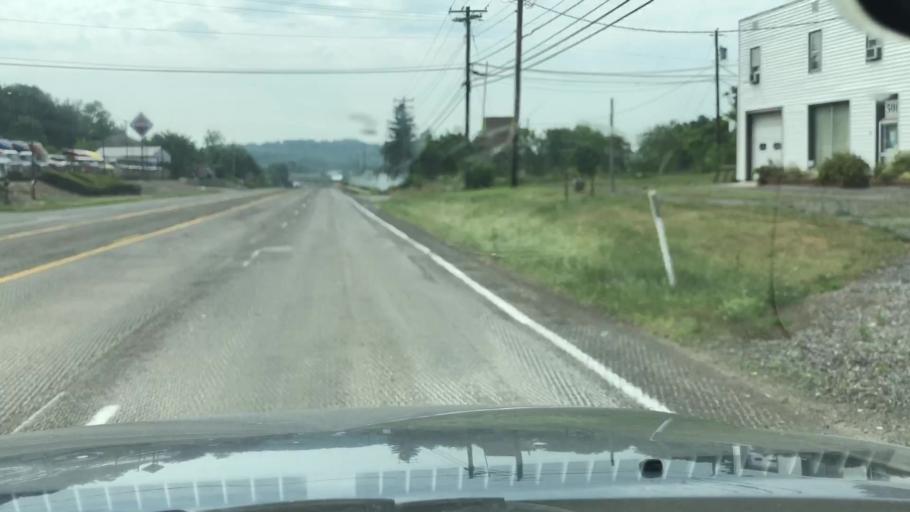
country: US
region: Pennsylvania
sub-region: Butler County
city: Nixon
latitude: 40.7697
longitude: -79.9271
